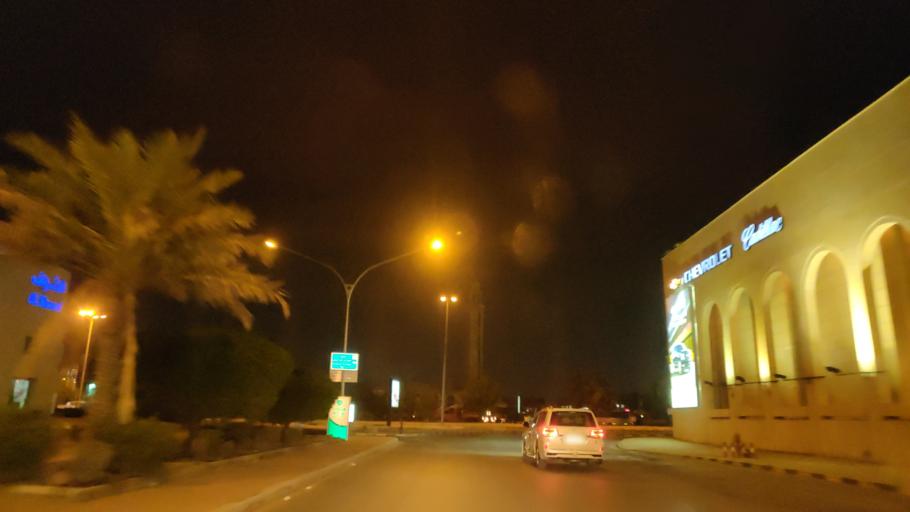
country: KW
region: Al Asimah
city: Ar Rabiyah
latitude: 29.3131
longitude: 47.9342
